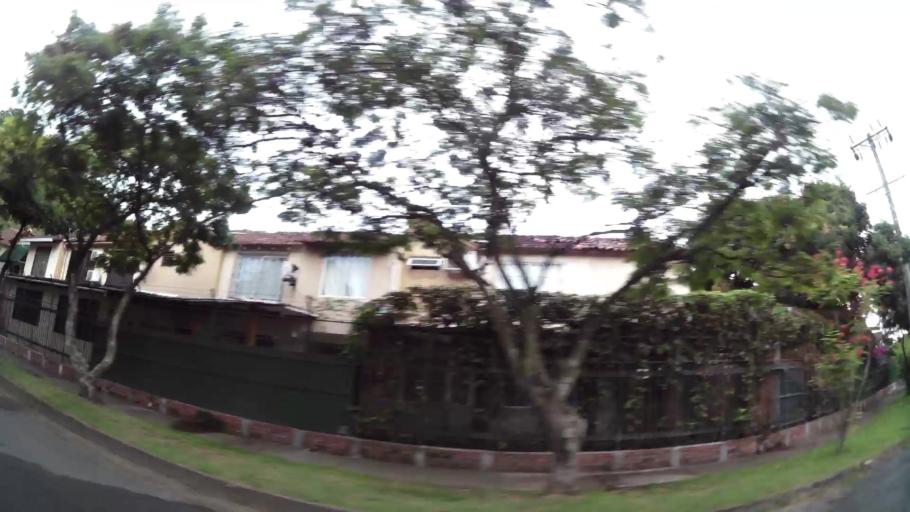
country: CO
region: Valle del Cauca
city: Cali
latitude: 3.4879
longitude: -76.5169
